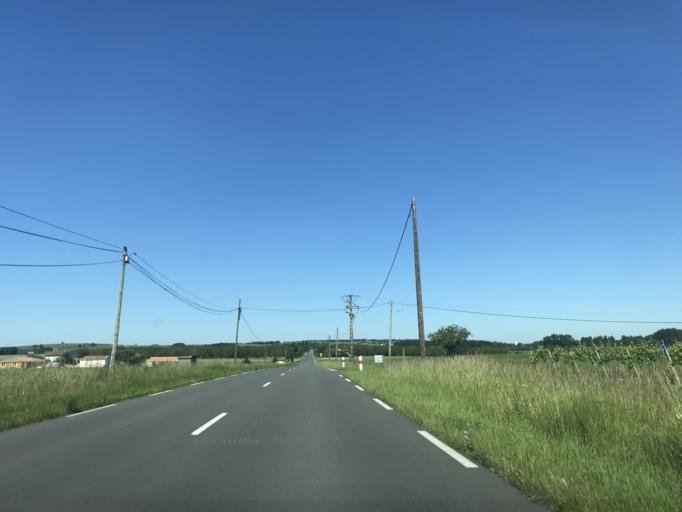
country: FR
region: Poitou-Charentes
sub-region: Departement de la Charente
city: Barbezieux-Saint-Hilaire
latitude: 45.4951
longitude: -0.2186
